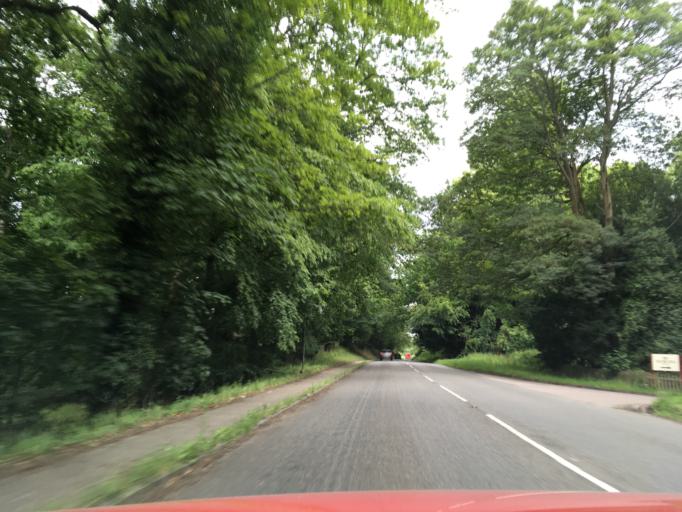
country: GB
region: England
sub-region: Central Bedfordshire
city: Aspley Guise
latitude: 51.9977
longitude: -0.6353
